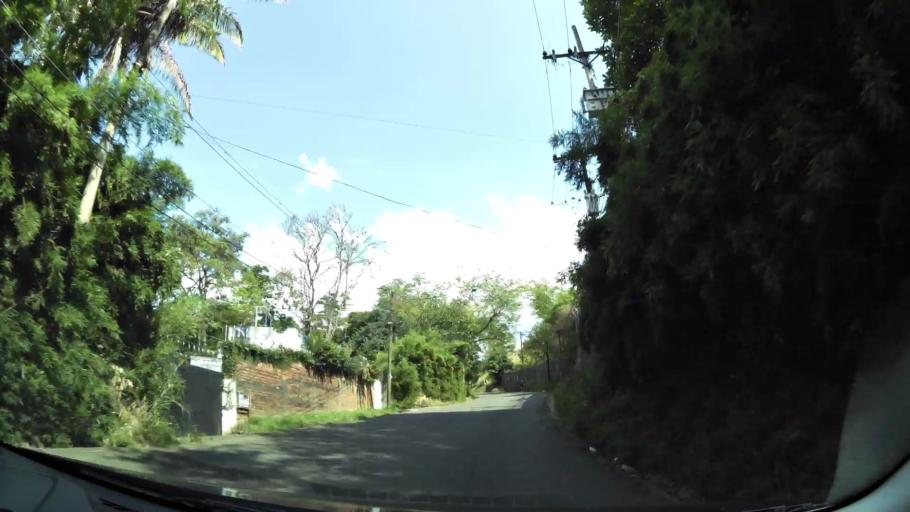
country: CO
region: Valle del Cauca
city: Cali
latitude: 3.4421
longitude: -76.5544
